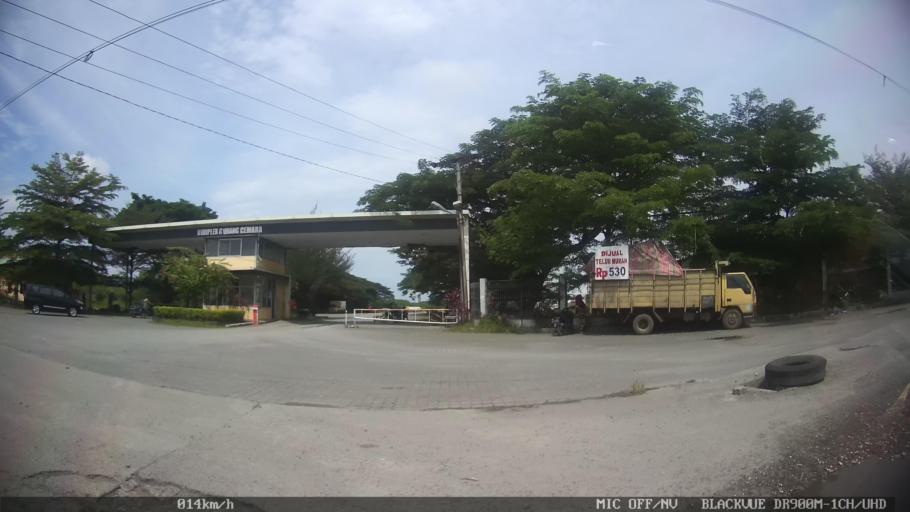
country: ID
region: North Sumatra
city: Medan
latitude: 3.6351
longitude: 98.7163
